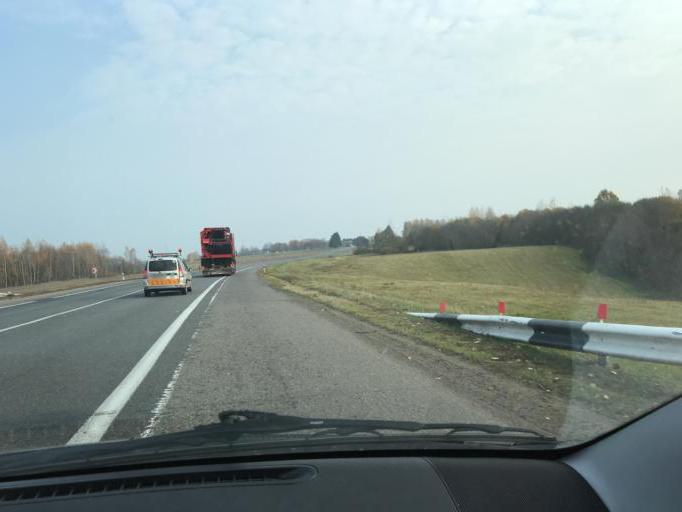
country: BY
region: Vitebsk
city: Haradok
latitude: 55.1453
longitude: 29.8383
